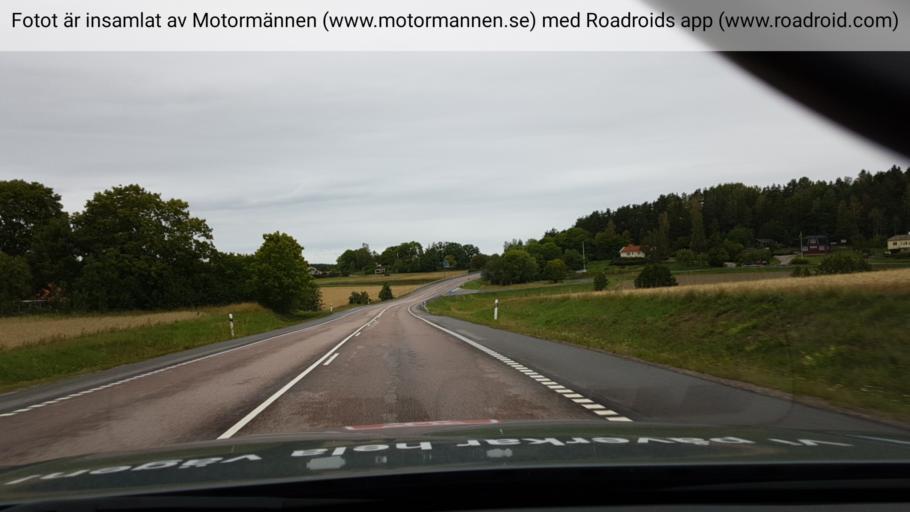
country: SE
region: Soedermanland
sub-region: Trosa Kommun
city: Vagnharad
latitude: 59.0160
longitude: 17.5931
